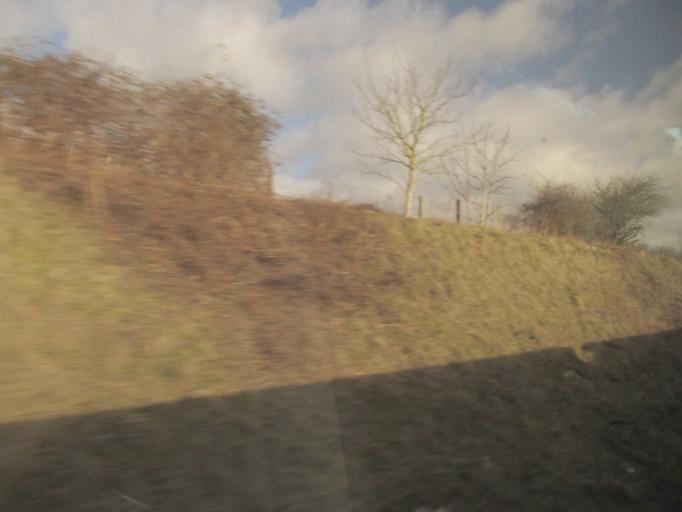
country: GB
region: England
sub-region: Royal Borough of Windsor and Maidenhead
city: White Waltham
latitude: 51.5056
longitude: -0.7700
